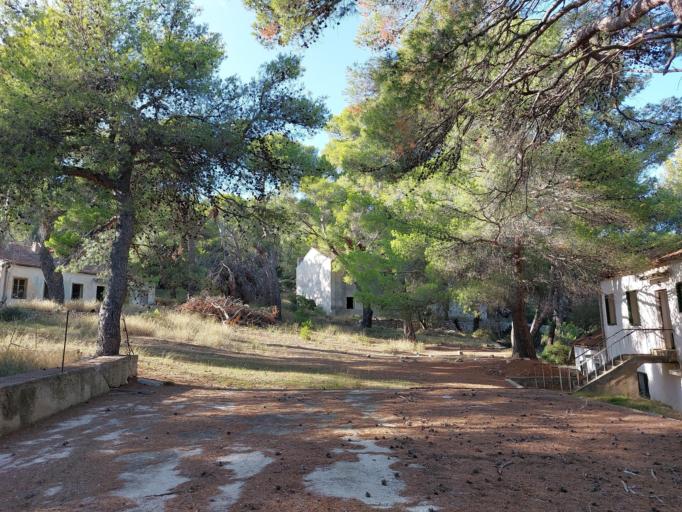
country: HR
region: Dubrovacko-Neretvanska
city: Smokvica
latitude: 42.7701
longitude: 16.7907
